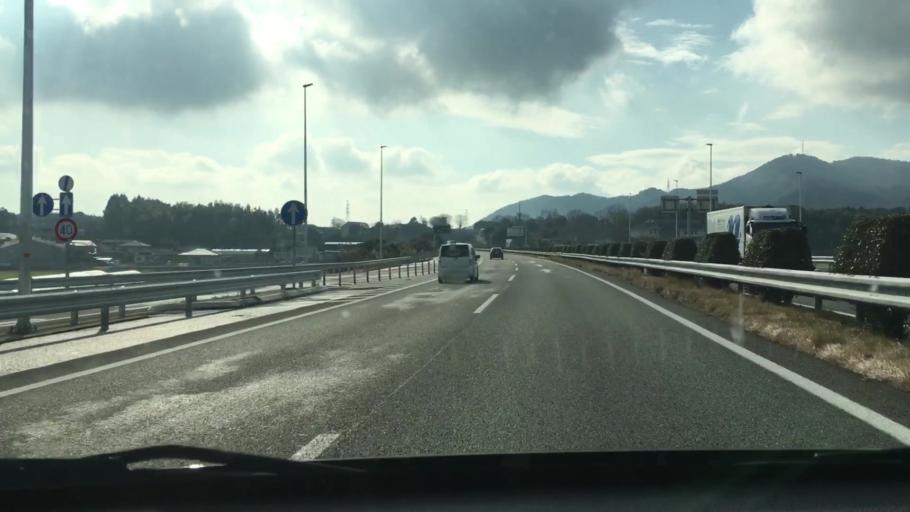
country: JP
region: Kumamoto
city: Uto
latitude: 32.6942
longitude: 130.7419
